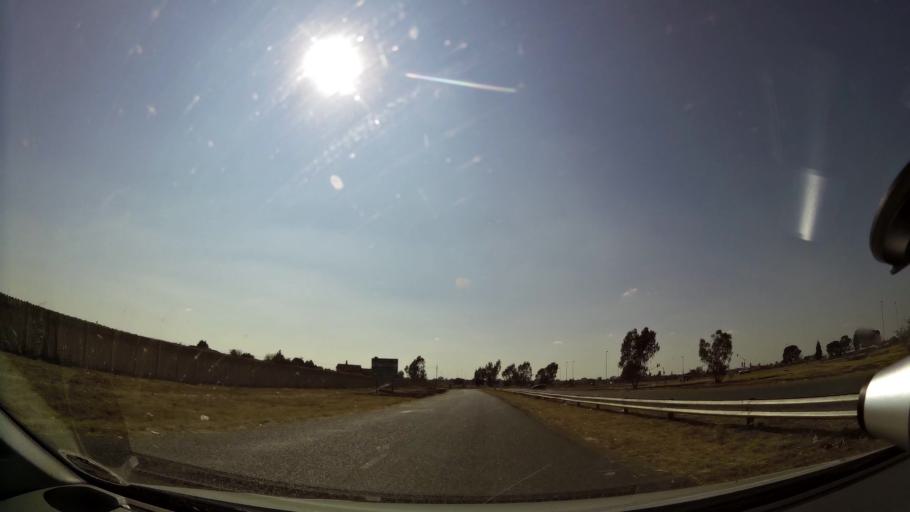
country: ZA
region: Orange Free State
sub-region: Mangaung Metropolitan Municipality
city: Bloemfontein
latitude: -29.1479
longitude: 26.2645
